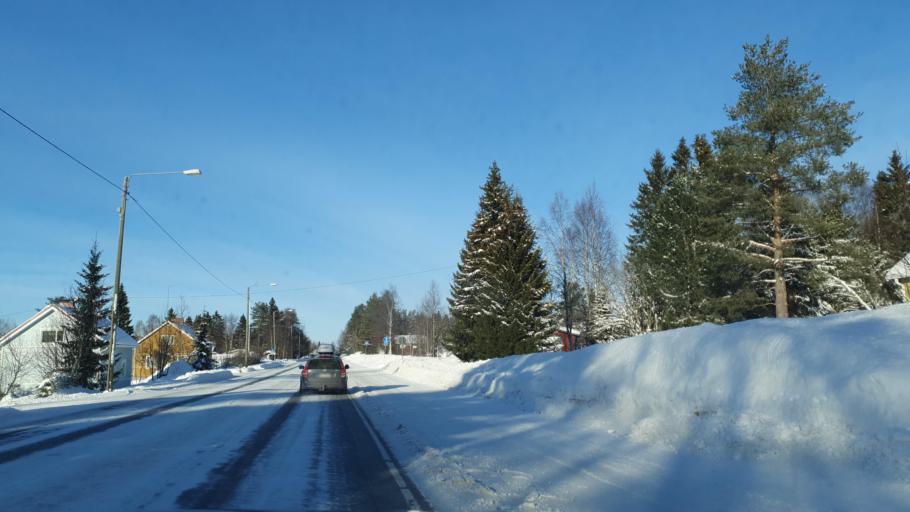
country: FI
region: Lapland
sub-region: Kemi-Tornio
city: Tornio
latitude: 66.0364
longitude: 24.0239
